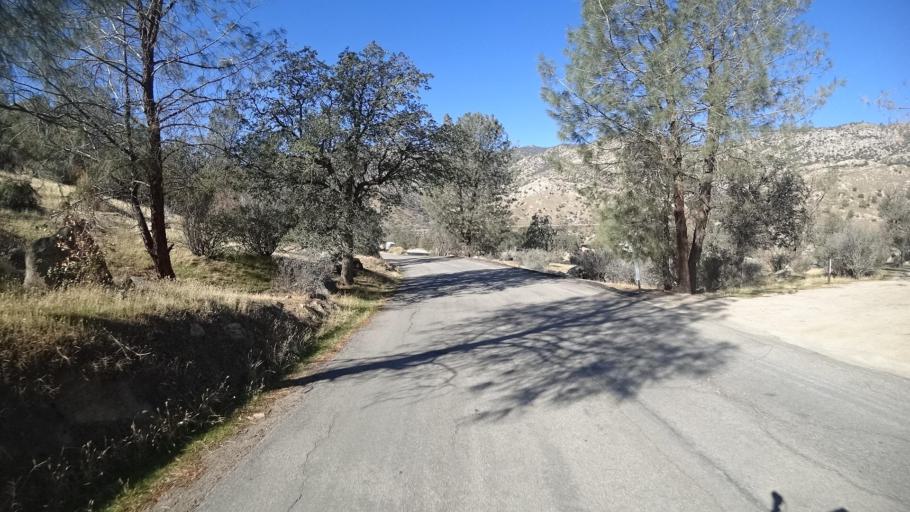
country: US
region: California
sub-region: Kern County
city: Bodfish
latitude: 35.5763
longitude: -118.5533
